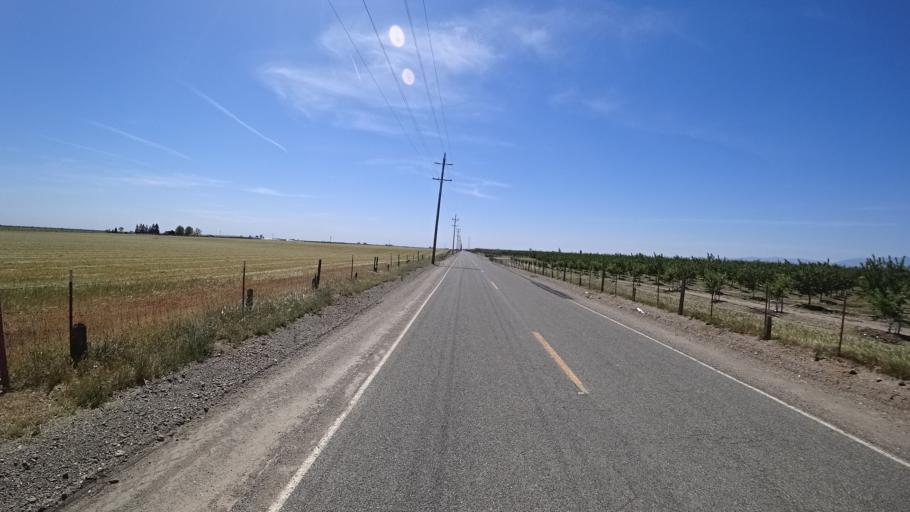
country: US
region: California
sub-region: Glenn County
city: Orland
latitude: 39.6666
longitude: -122.1782
